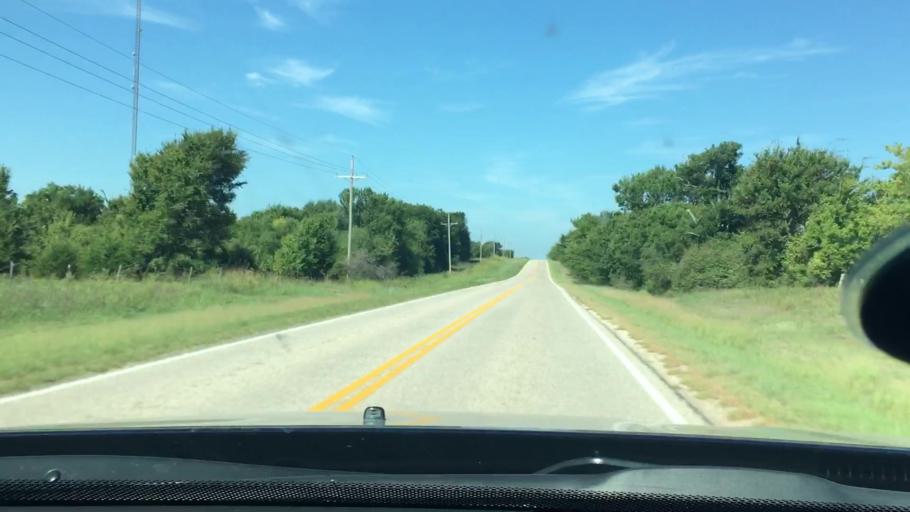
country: US
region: Oklahoma
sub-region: Johnston County
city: Tishomingo
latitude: 34.3614
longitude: -96.5531
